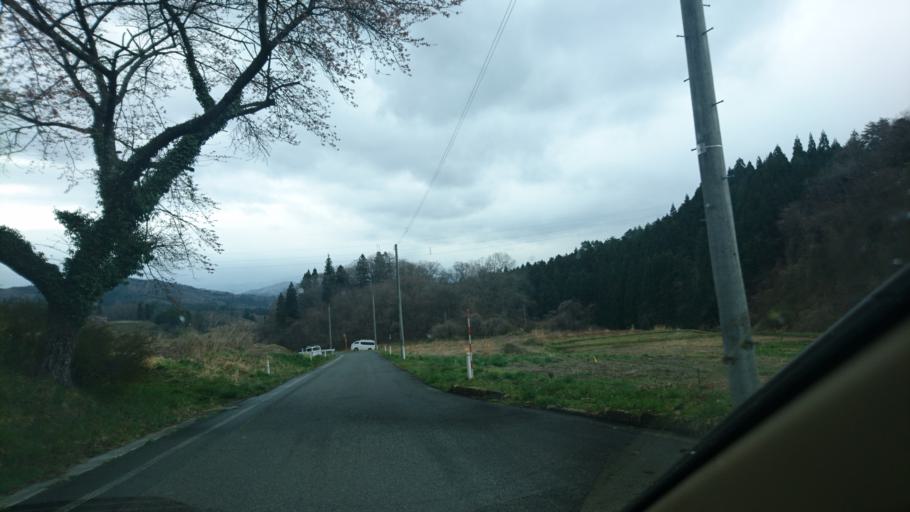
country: JP
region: Iwate
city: Ichinoseki
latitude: 38.9487
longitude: 141.3002
